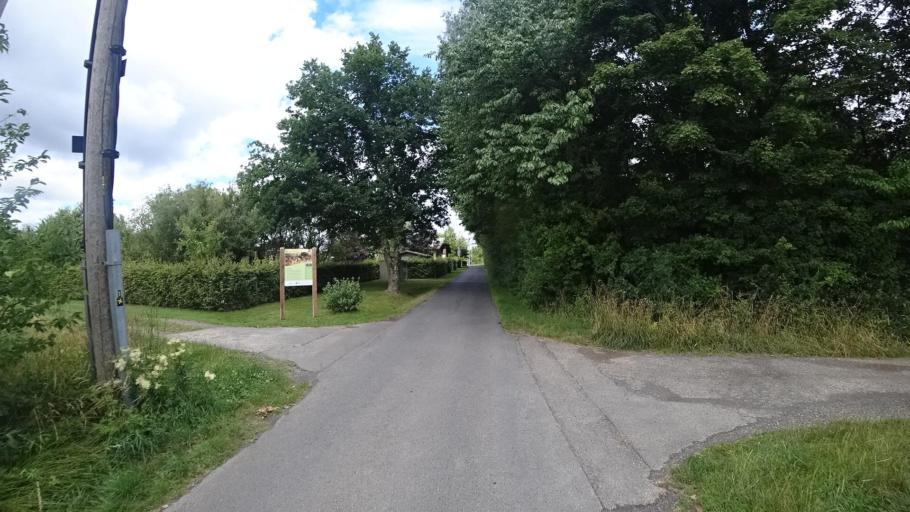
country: DE
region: Rheinland-Pfalz
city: Kircheib
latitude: 50.7081
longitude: 7.4533
